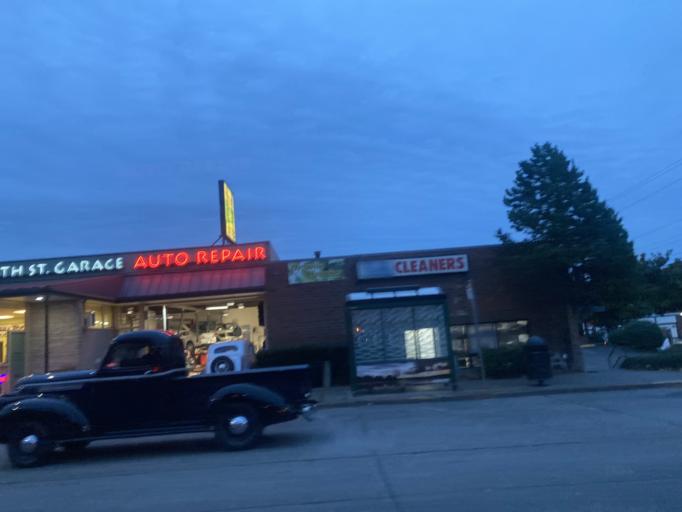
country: US
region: Washington
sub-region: King County
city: Seattle
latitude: 47.6399
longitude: -122.4010
